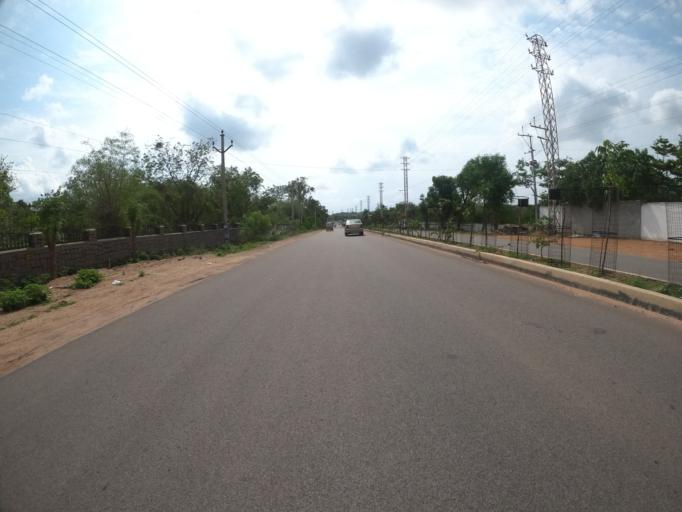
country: IN
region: Telangana
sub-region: Medak
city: Serilingampalle
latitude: 17.3925
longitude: 78.3220
